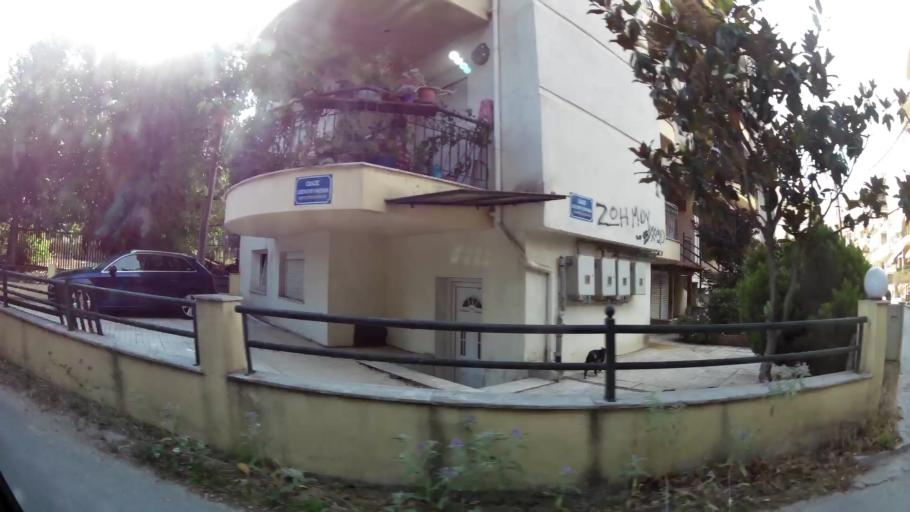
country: GR
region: Central Macedonia
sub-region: Nomos Thessalonikis
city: Kalamaria
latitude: 40.5675
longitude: 22.9696
